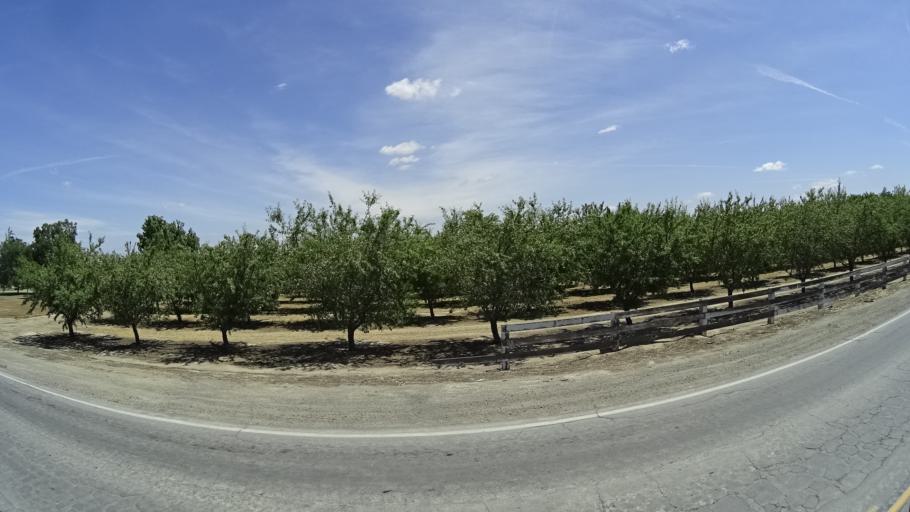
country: US
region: California
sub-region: Kings County
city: Home Garden
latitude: 36.2995
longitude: -119.6728
